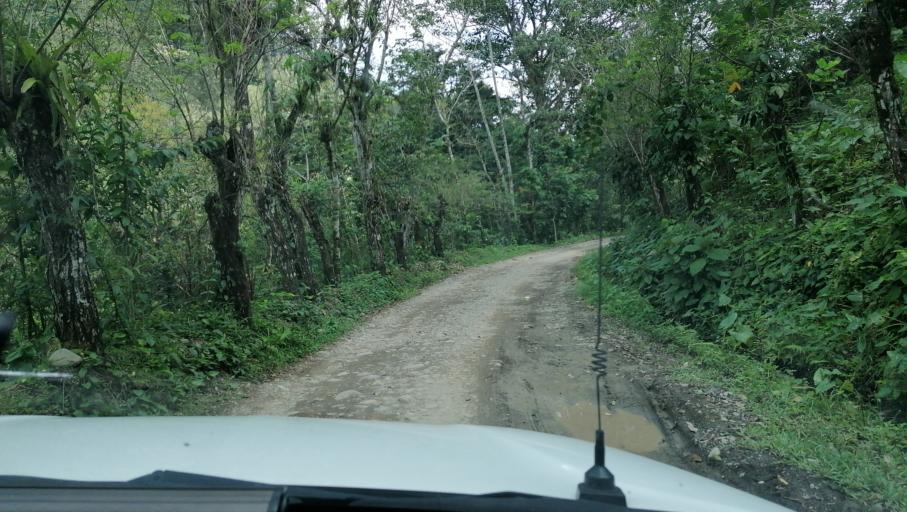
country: MX
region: Chiapas
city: Ixtacomitan
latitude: 17.4442
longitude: -93.1782
